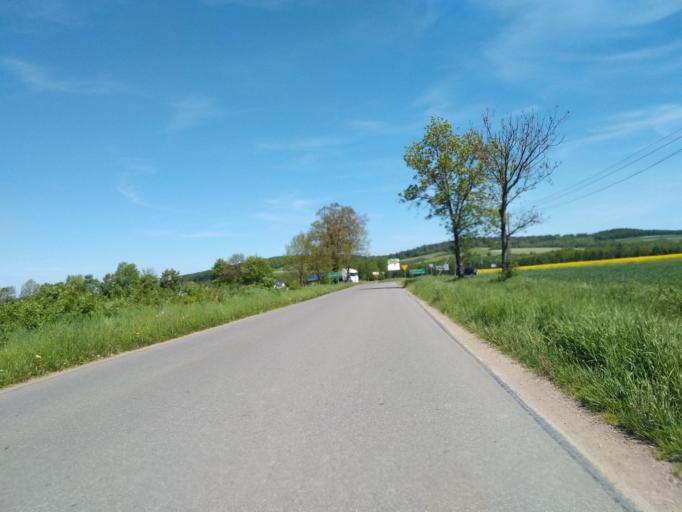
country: PL
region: Subcarpathian Voivodeship
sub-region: Powiat krosnienski
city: Sieniawa
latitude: 49.5498
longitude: 21.9401
